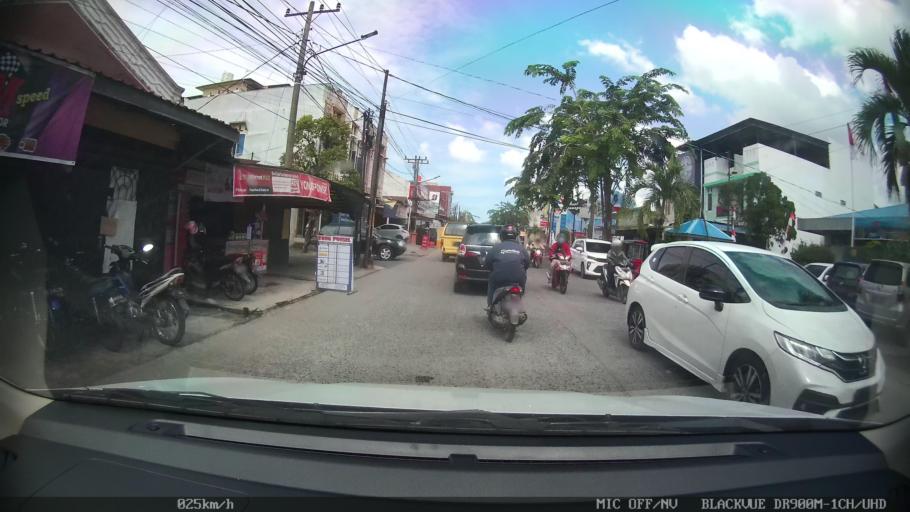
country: ID
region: North Sumatra
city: Sunggal
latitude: 3.6052
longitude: 98.6316
